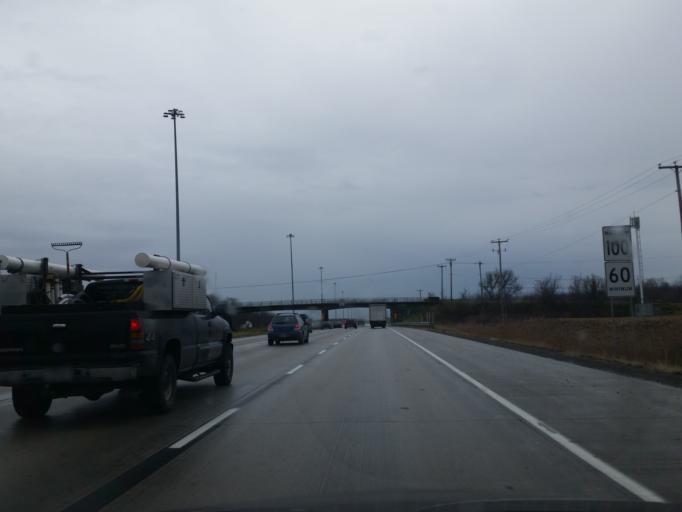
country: CA
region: Quebec
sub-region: Laurentides
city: Blainville
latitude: 45.7060
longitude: -73.9580
